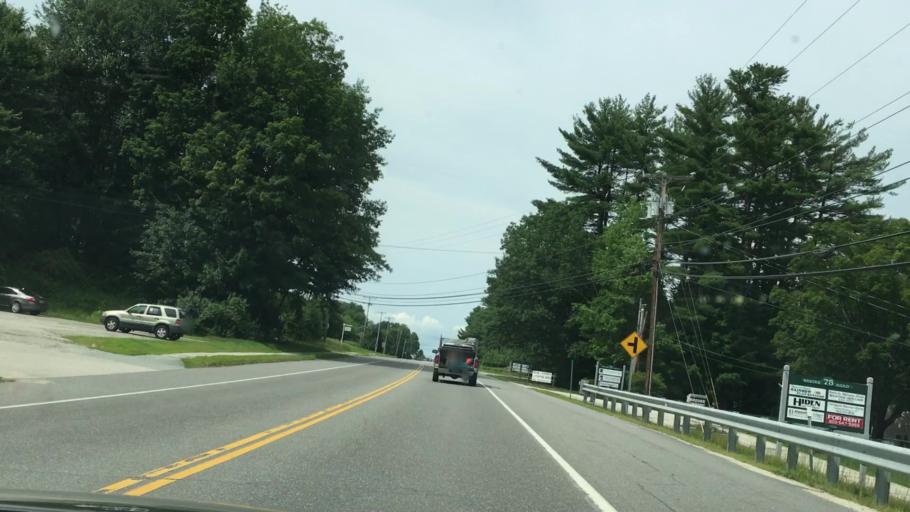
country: US
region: New Hampshire
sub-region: Hillsborough County
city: Peterborough
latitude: 42.9040
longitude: -71.9367
